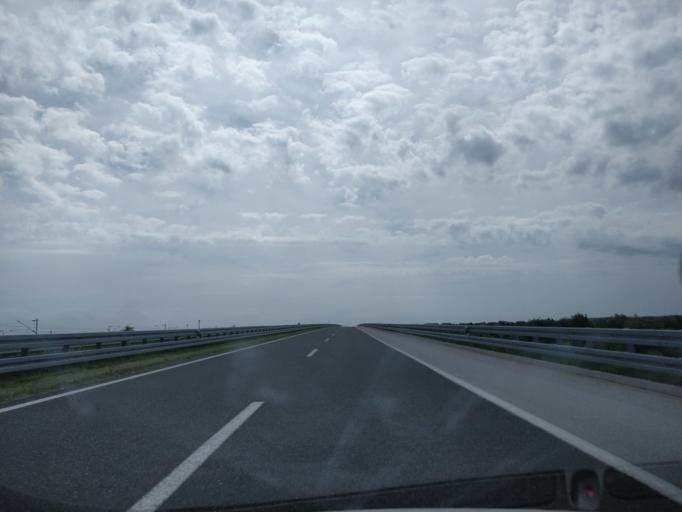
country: HR
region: Zagrebacka
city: Gradici
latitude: 45.7178
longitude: 16.0331
